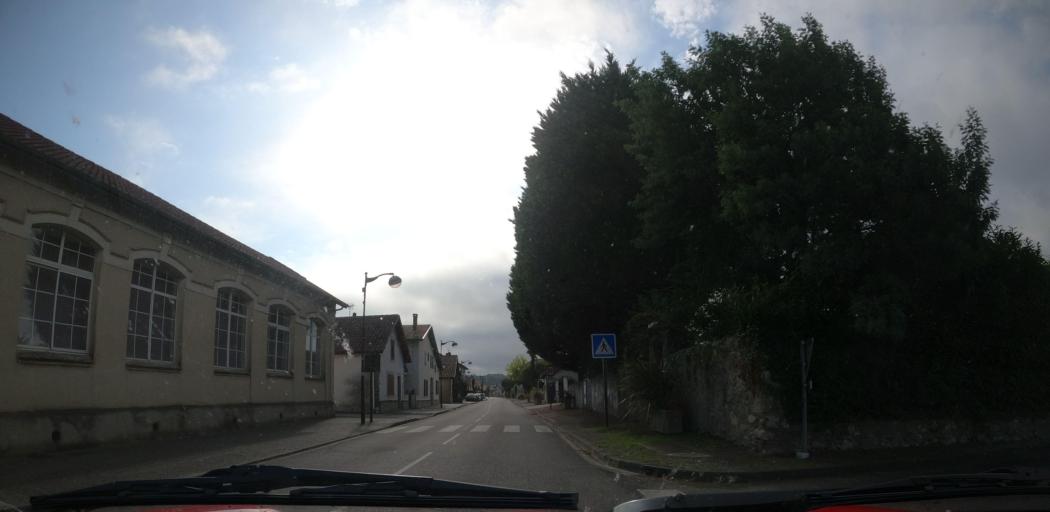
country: FR
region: Aquitaine
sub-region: Departement des Landes
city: Peyrehorade
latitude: 43.5309
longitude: -1.0599
